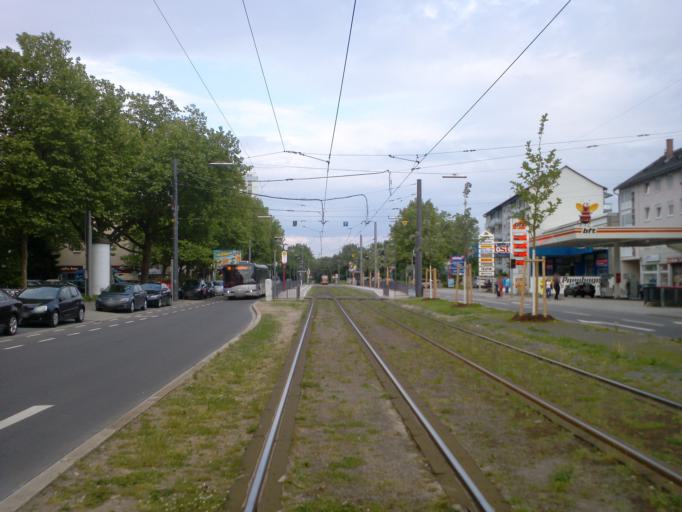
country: DE
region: Baden-Wuerttemberg
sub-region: Karlsruhe Region
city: Karlsruhe
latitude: 49.0113
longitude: 8.3572
